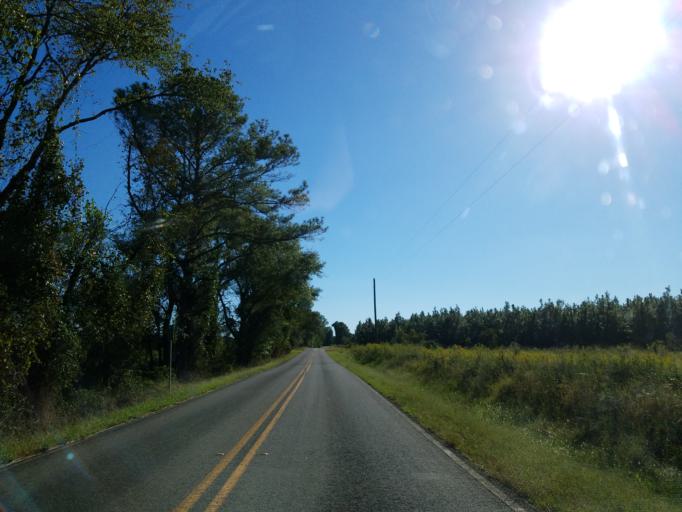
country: US
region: Georgia
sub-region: Dooly County
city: Vienna
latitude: 32.2136
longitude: -83.8942
